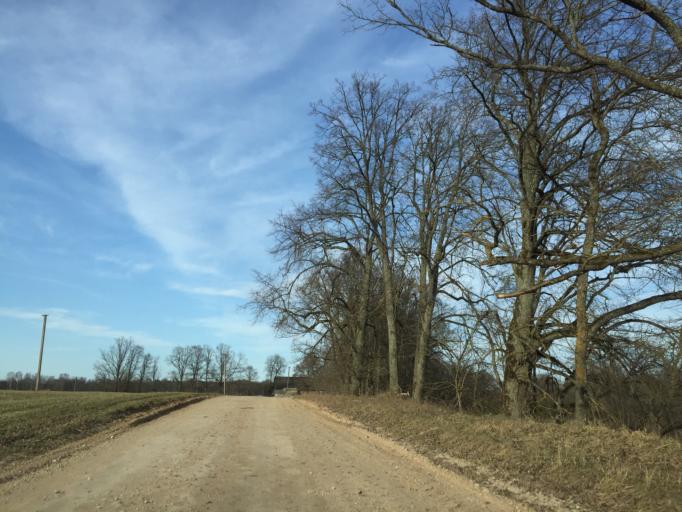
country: LV
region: Kegums
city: Kegums
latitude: 56.7974
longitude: 24.7322
